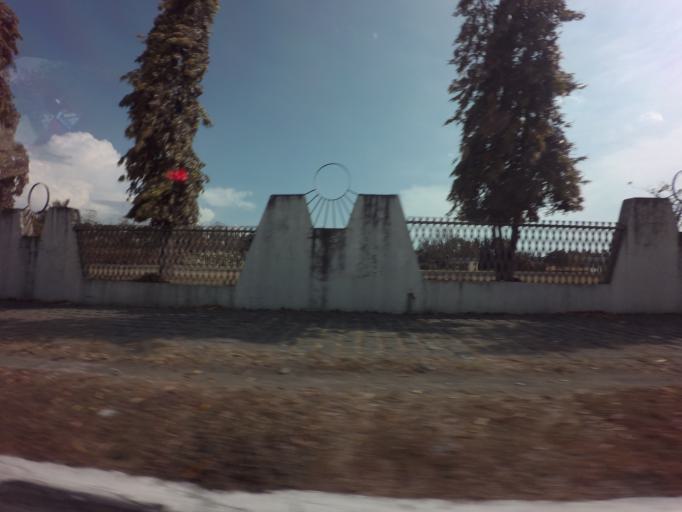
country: PH
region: Calabarzon
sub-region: Province of Rizal
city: Taguig
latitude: 14.5191
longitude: 121.0501
